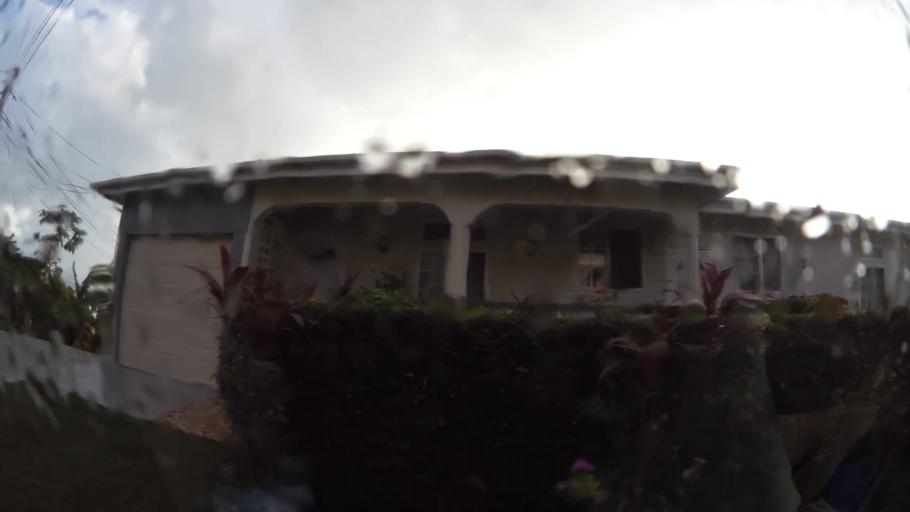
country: DM
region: Saint Paul
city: Mahaut
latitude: 15.3647
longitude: -61.3983
